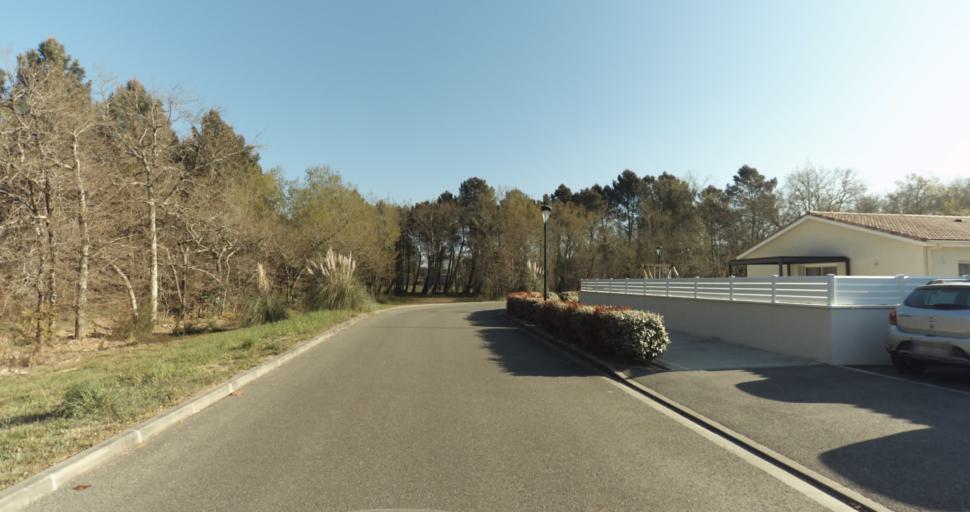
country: FR
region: Aquitaine
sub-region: Departement de la Gironde
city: Martignas-sur-Jalle
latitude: 44.8037
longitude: -0.7968
